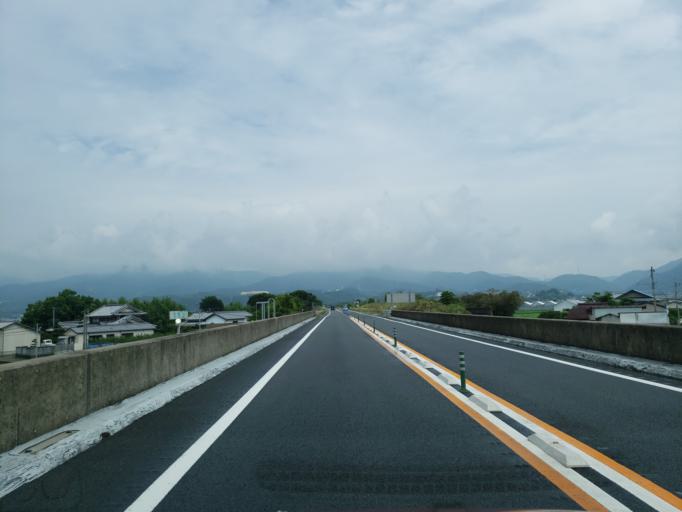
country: JP
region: Tokushima
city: Ishii
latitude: 34.1289
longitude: 134.4621
